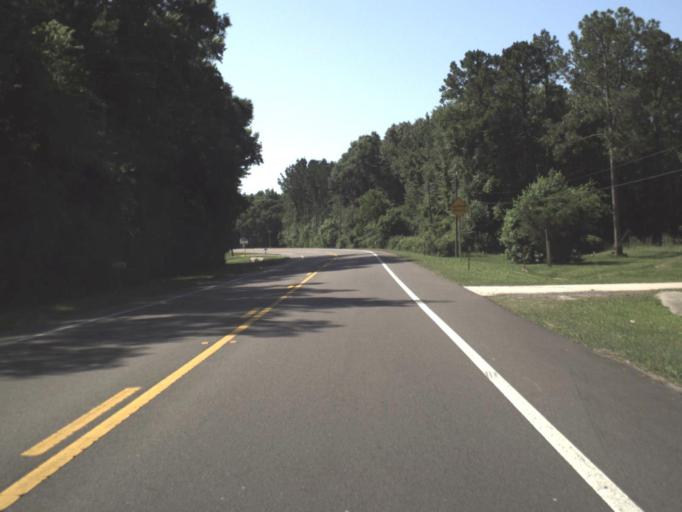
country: US
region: Florida
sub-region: Nassau County
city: Nassau Village-Ratliff
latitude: 30.5224
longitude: -81.7687
